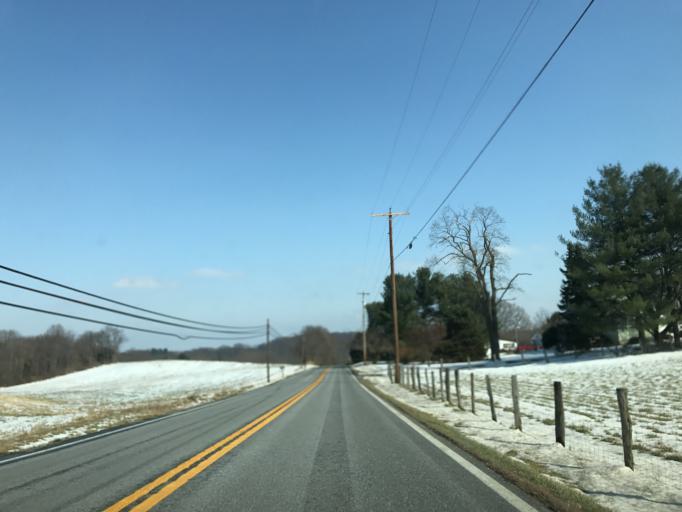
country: US
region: Pennsylvania
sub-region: York County
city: Susquehanna Trails
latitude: 39.6969
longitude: -76.4358
